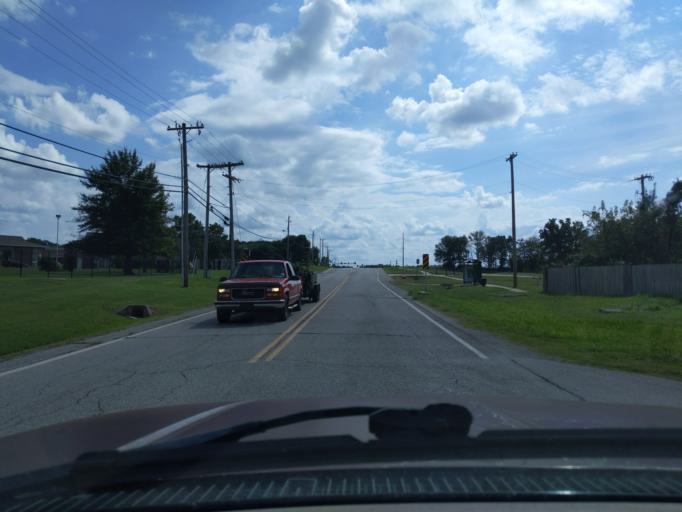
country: US
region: Oklahoma
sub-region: Tulsa County
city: Oakhurst
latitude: 36.0788
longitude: -96.0117
